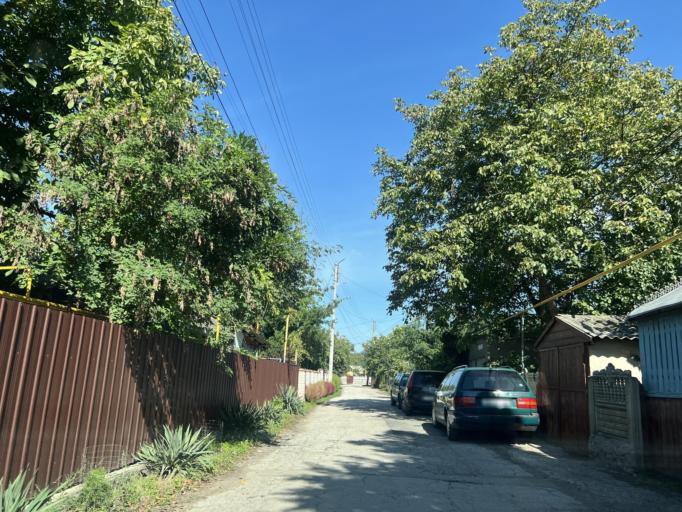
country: RO
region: Iasi
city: Ungheni-Prut
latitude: 47.1958
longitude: 27.7884
